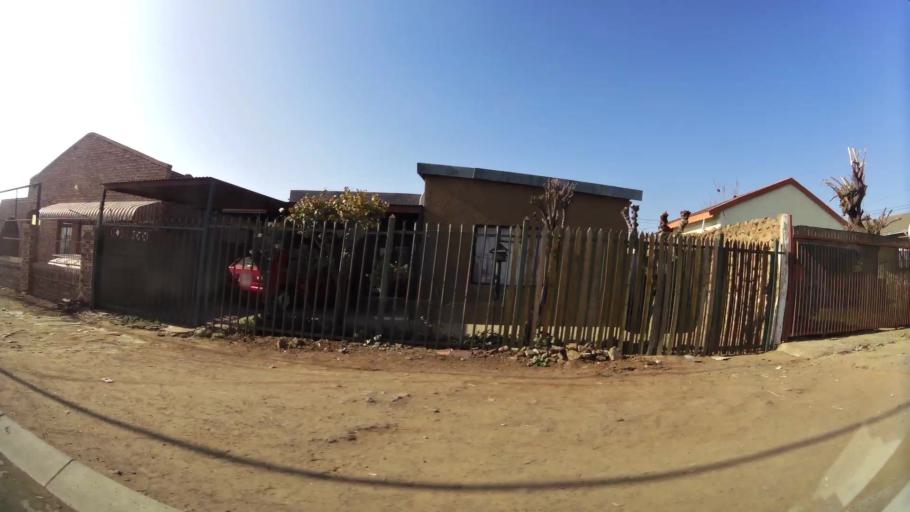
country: ZA
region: Orange Free State
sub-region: Mangaung Metropolitan Municipality
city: Bloemfontein
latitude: -29.1748
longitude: 26.2284
